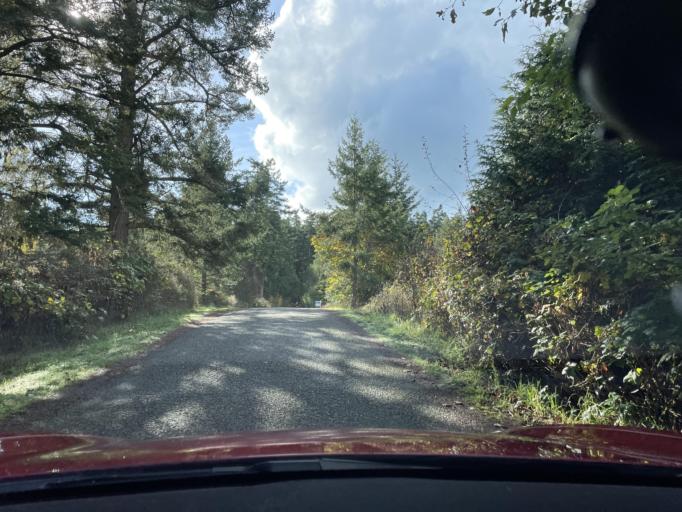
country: US
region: Washington
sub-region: San Juan County
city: Friday Harbor
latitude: 48.5000
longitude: -123.0230
